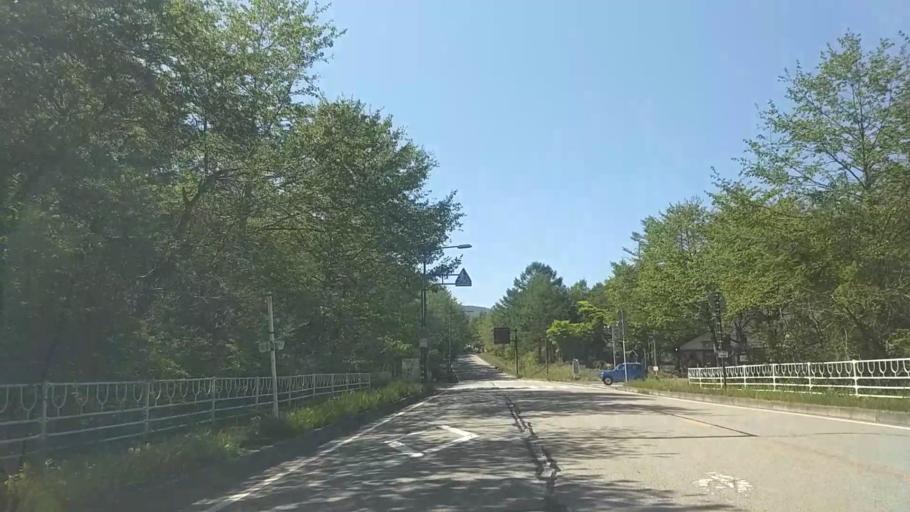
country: JP
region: Yamanashi
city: Nirasaki
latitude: 35.9216
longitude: 138.4344
